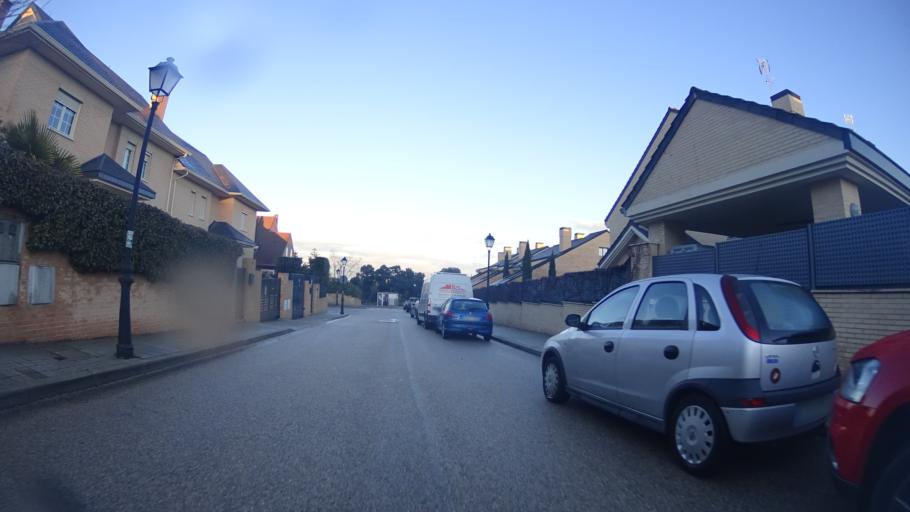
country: ES
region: Madrid
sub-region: Provincia de Madrid
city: Torrelodones
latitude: 40.5756
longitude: -3.9173
